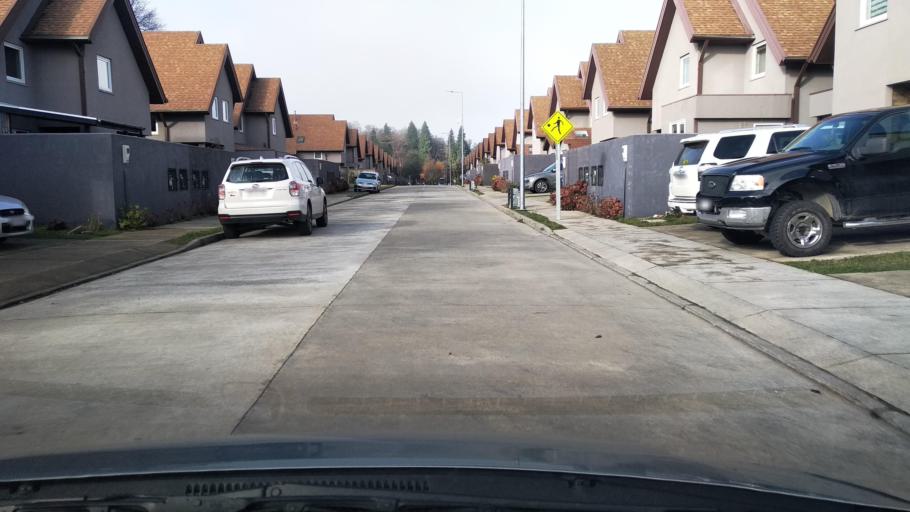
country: CL
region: Los Rios
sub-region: Provincia de Valdivia
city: Valdivia
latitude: -39.8099
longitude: -73.2620
